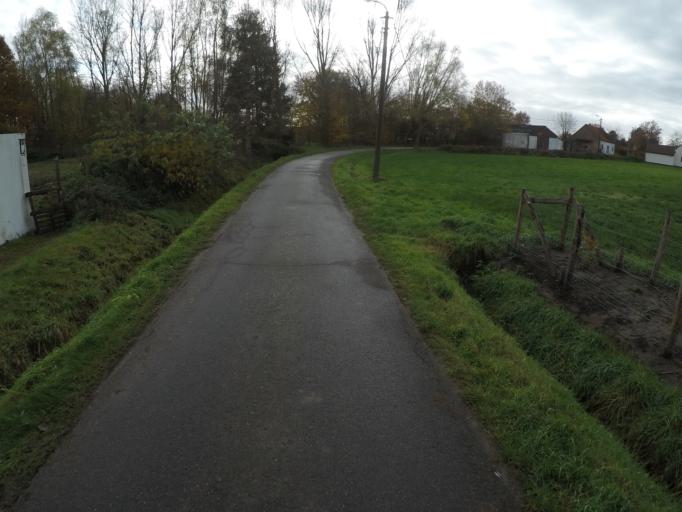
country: BE
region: Flanders
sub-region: Provincie Vlaams-Brabant
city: Londerzeel
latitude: 51.0174
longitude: 4.2988
